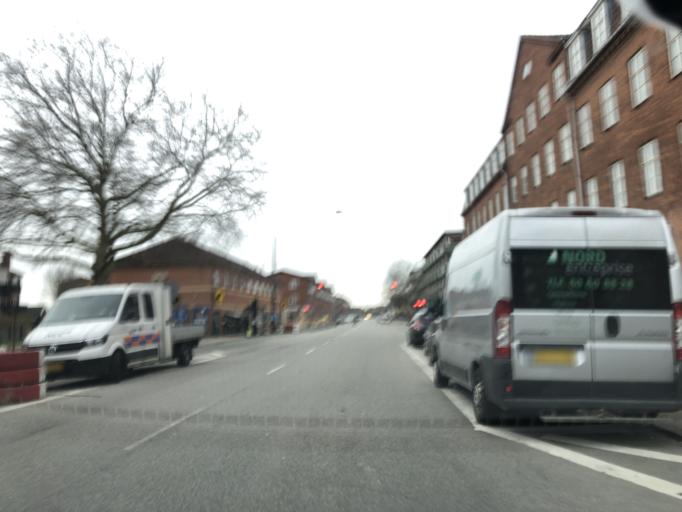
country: DK
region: Capital Region
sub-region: Tarnby Kommune
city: Tarnby
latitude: 55.6517
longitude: 12.6204
